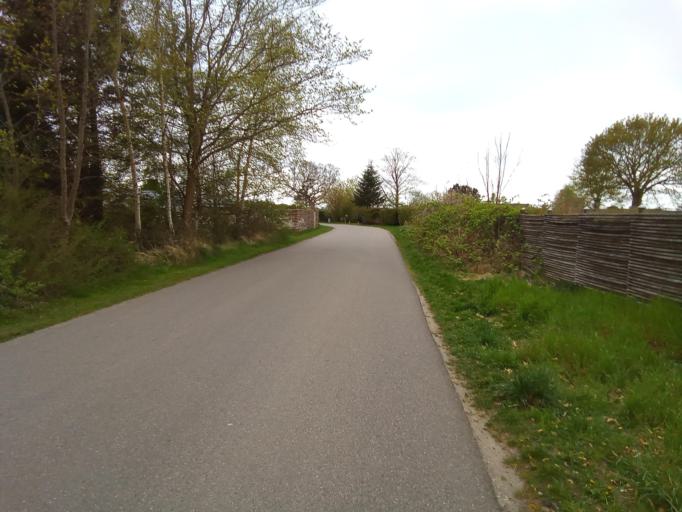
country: DK
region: Capital Region
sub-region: Frederikssund Kommune
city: Frederikssund
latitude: 55.8940
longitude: 12.0587
